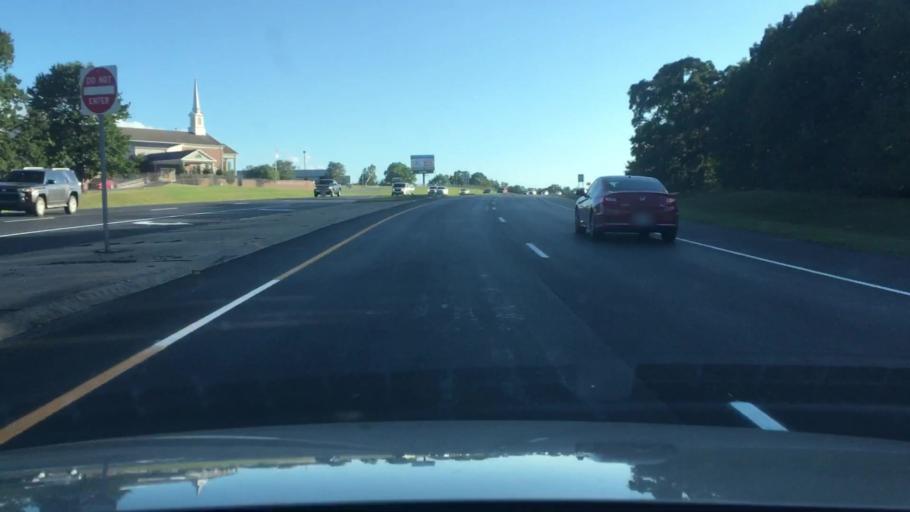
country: US
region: Oklahoma
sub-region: Cherokee County
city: Tahlequah
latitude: 35.9125
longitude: -94.9555
